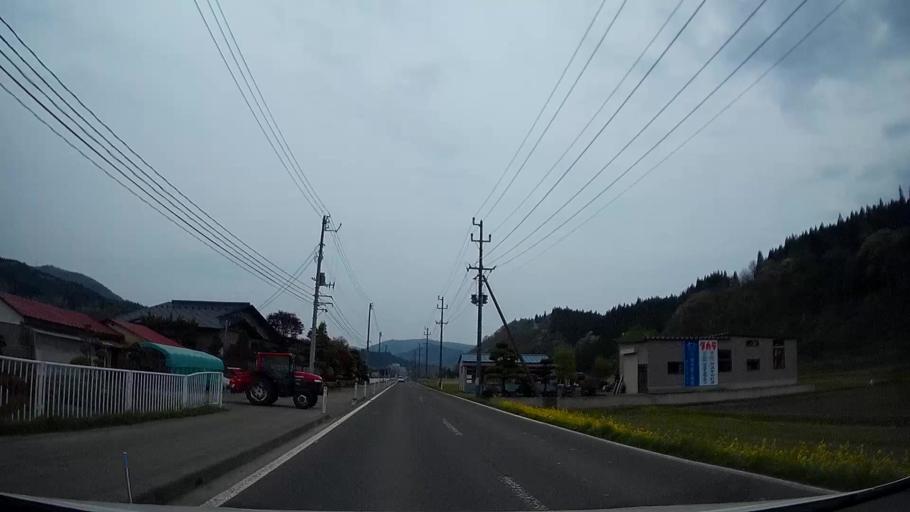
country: JP
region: Akita
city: Hanawa
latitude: 40.2888
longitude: 140.8107
